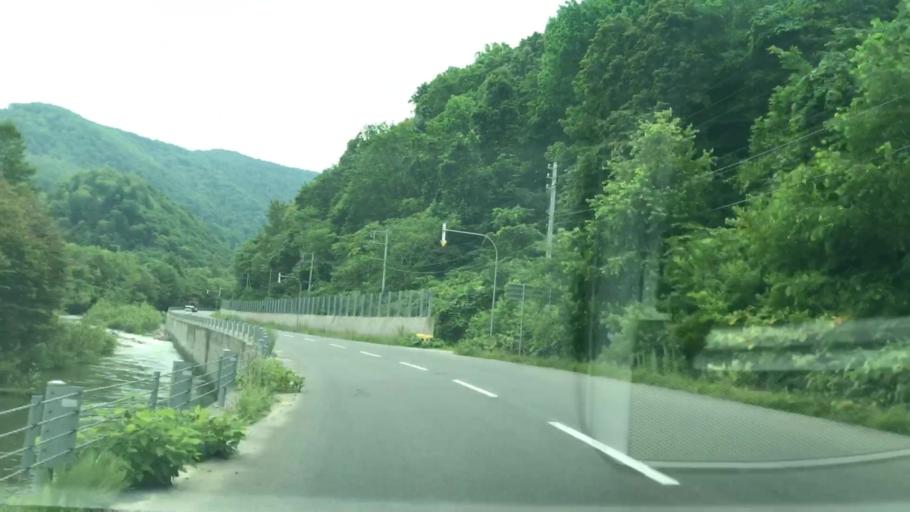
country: JP
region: Hokkaido
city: Yoichi
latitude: 43.0385
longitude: 140.8601
